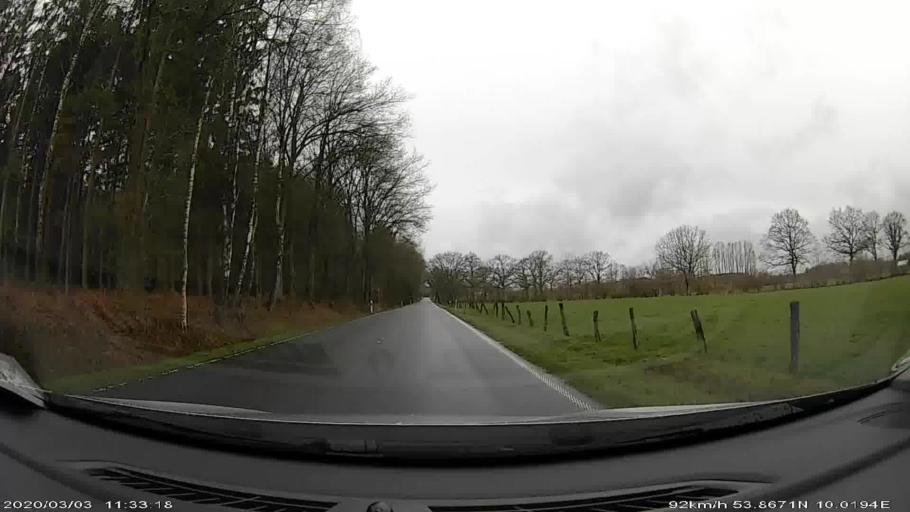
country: DE
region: Schleswig-Holstein
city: Kattendorf
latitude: 53.8683
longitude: 10.0140
